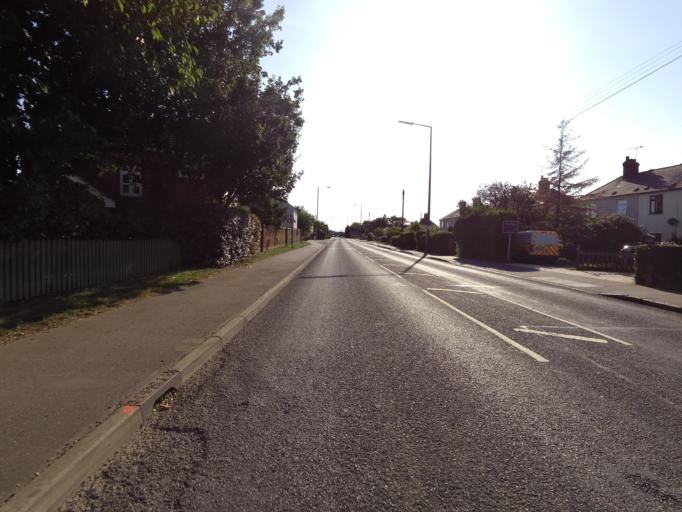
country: GB
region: England
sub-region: Essex
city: Hatfield Peverel
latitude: 51.7613
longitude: 0.5389
